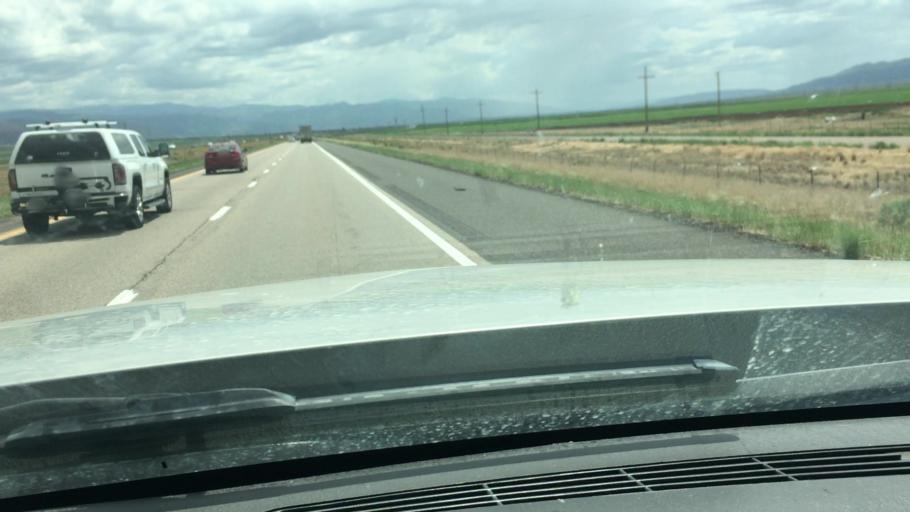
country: US
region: Utah
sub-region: Beaver County
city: Beaver
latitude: 38.0507
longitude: -112.7002
